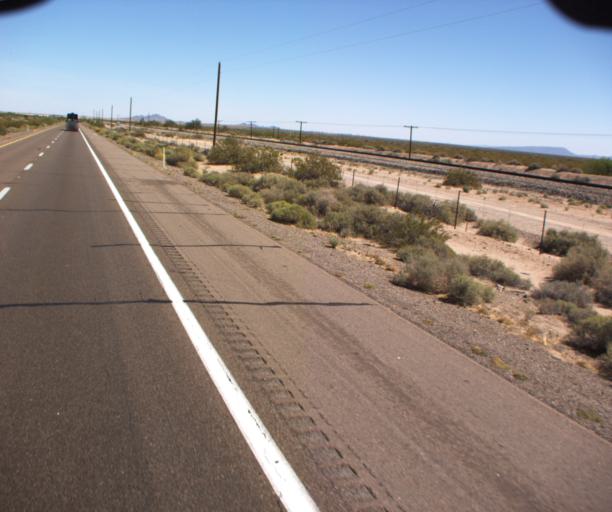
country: US
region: Arizona
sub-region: Yuma County
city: Wellton
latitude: 32.7464
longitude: -113.6722
